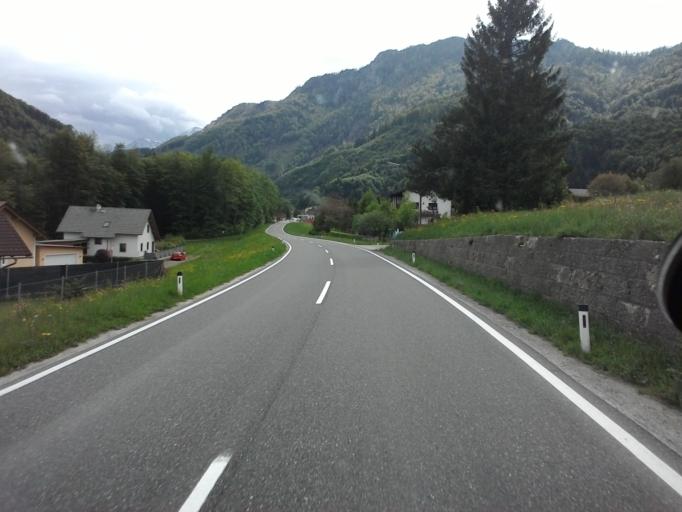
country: AT
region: Upper Austria
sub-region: Politischer Bezirk Kirchdorf an der Krems
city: Micheldorf in Oberoesterreich
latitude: 47.8372
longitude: 14.1604
